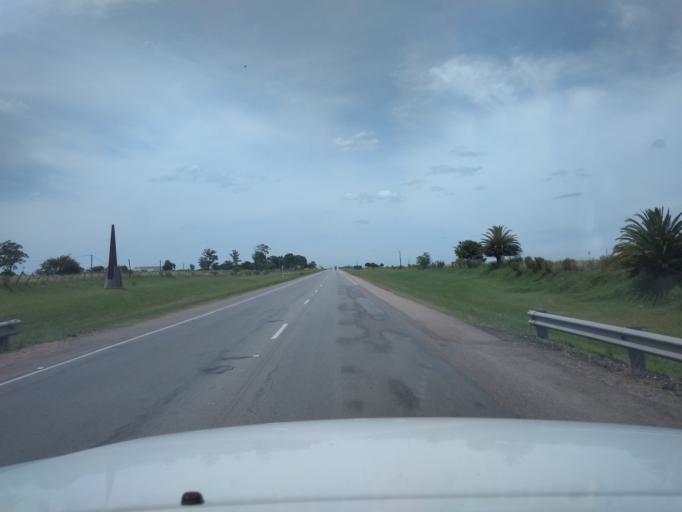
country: UY
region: Florida
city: Cardal
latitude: -34.3575
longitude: -56.2489
